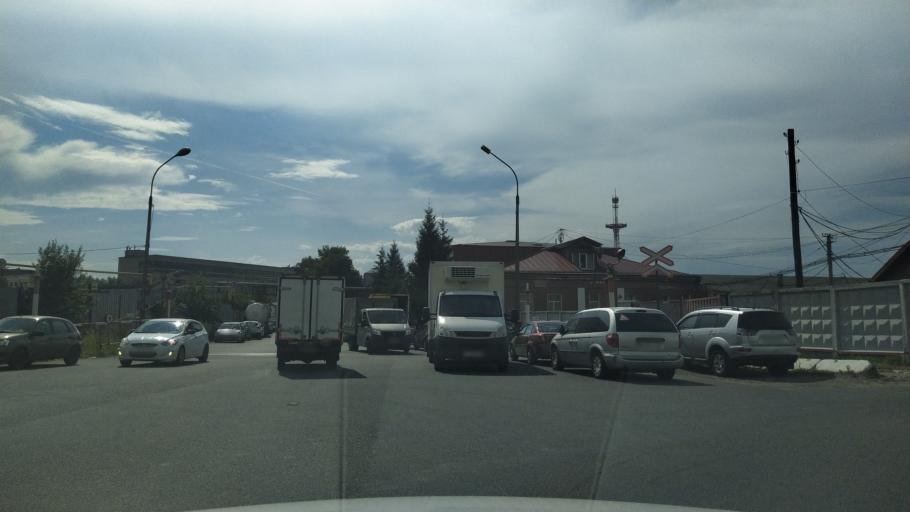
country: RU
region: Leningrad
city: Finlyandskiy
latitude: 59.9656
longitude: 30.3668
